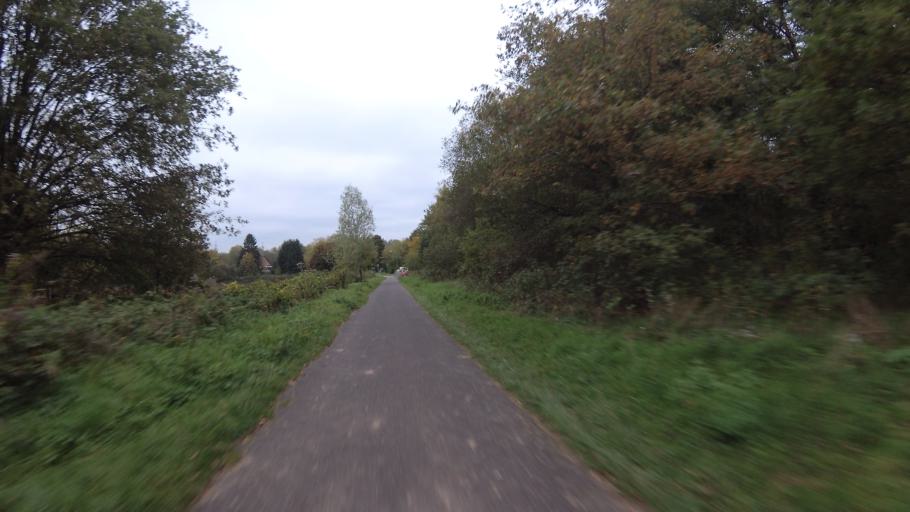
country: DE
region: Saarland
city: Homburg
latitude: 49.2991
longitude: 7.3198
